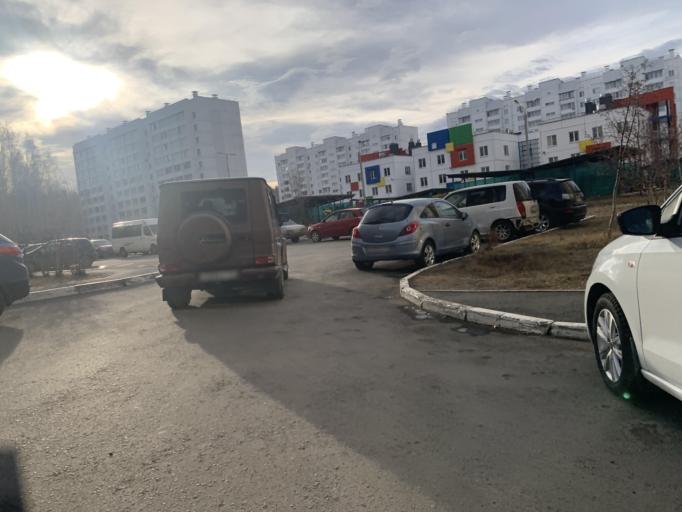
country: RU
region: Chelyabinsk
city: Roshchino
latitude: 55.2076
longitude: 61.3069
